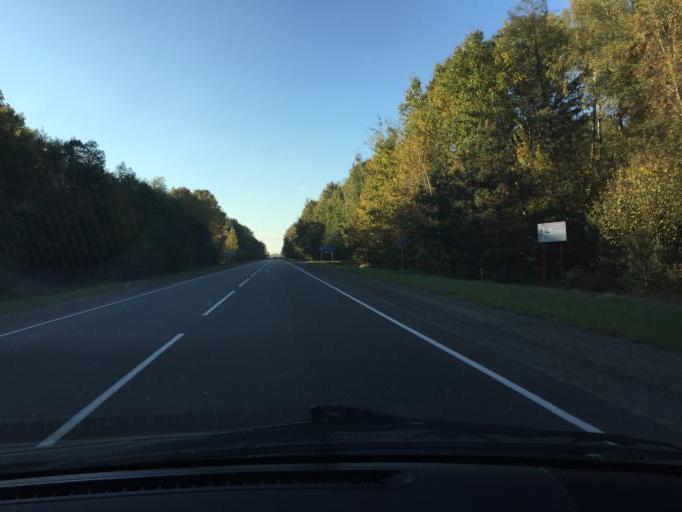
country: BY
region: Brest
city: Horad Luninyets
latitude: 52.3071
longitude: 26.6882
